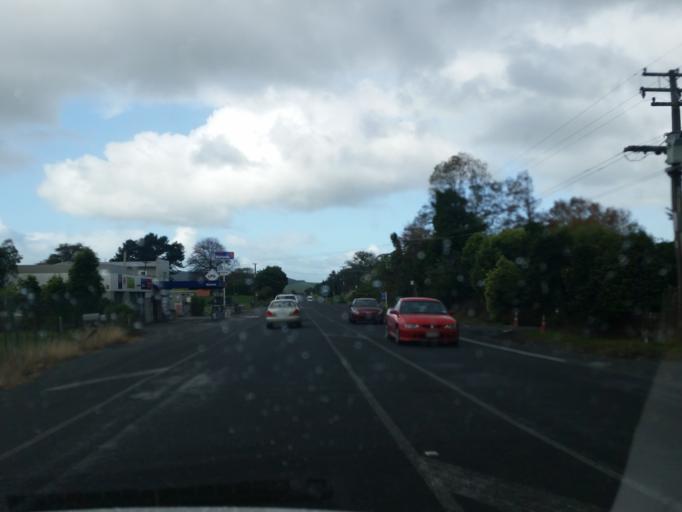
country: NZ
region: Waikato
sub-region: Waikato District
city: Te Kauwhata
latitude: -37.2490
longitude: 175.2210
